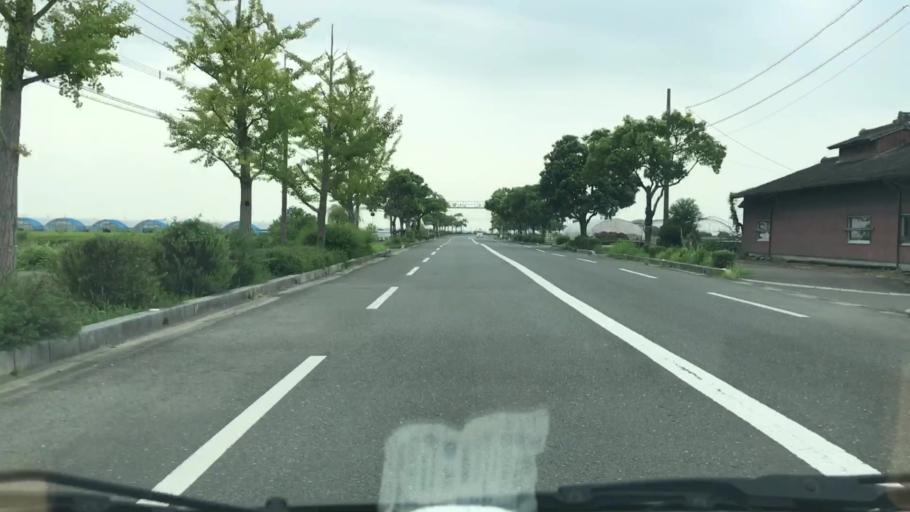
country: JP
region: Saga Prefecture
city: Okawa
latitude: 33.1948
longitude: 130.3036
